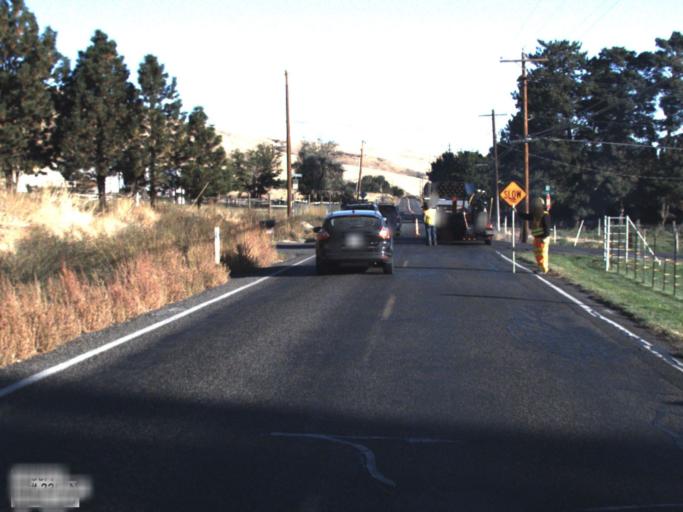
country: US
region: Washington
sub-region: Benton County
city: Benton City
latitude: 46.3155
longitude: -119.4932
